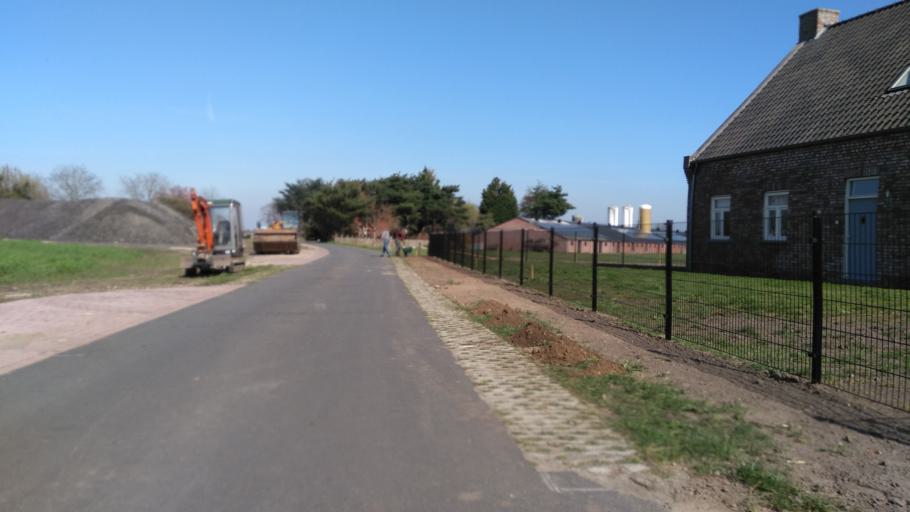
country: NL
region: North Brabant
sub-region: Gemeente Baarle-Nassau
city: Baarle-Nassau
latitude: 51.4391
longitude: 4.9419
